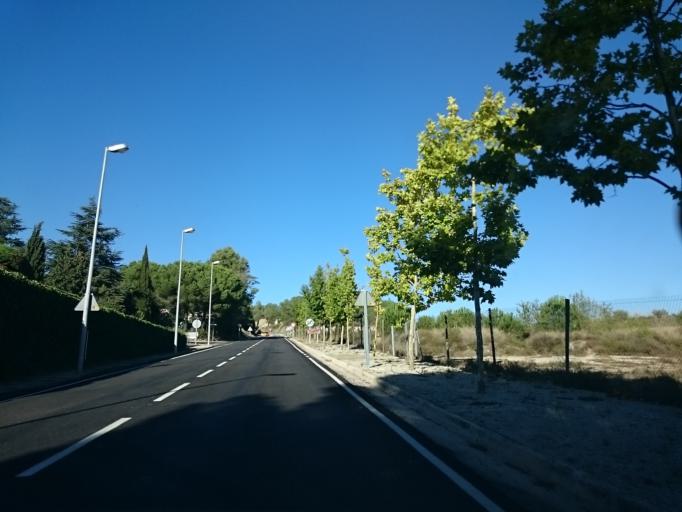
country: ES
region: Catalonia
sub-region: Provincia de Barcelona
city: Capellades
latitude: 41.5208
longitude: 1.7103
